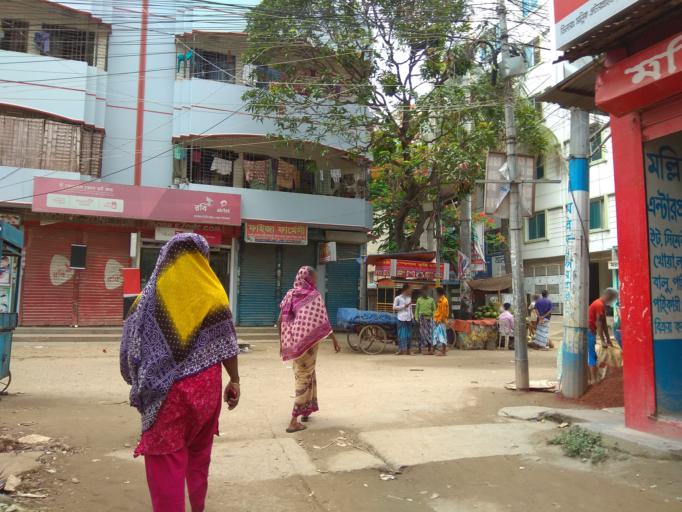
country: BD
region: Dhaka
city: Tungi
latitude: 23.8162
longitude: 90.3712
